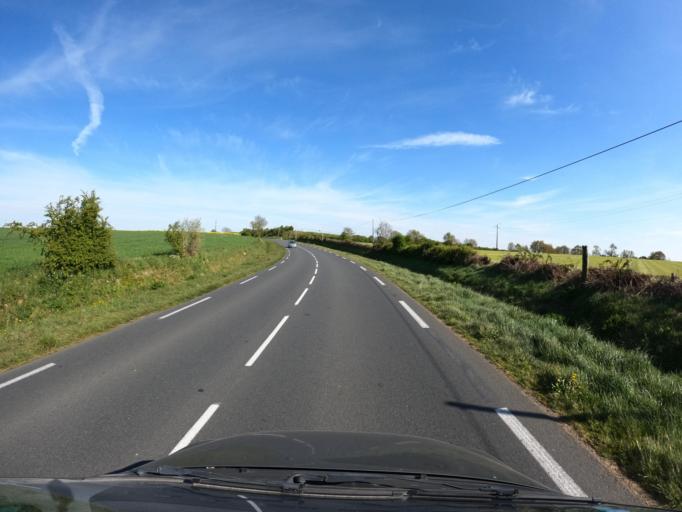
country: FR
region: Pays de la Loire
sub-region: Departement de Maine-et-Loire
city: La Seguiniere
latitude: 47.0695
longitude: -0.9161
